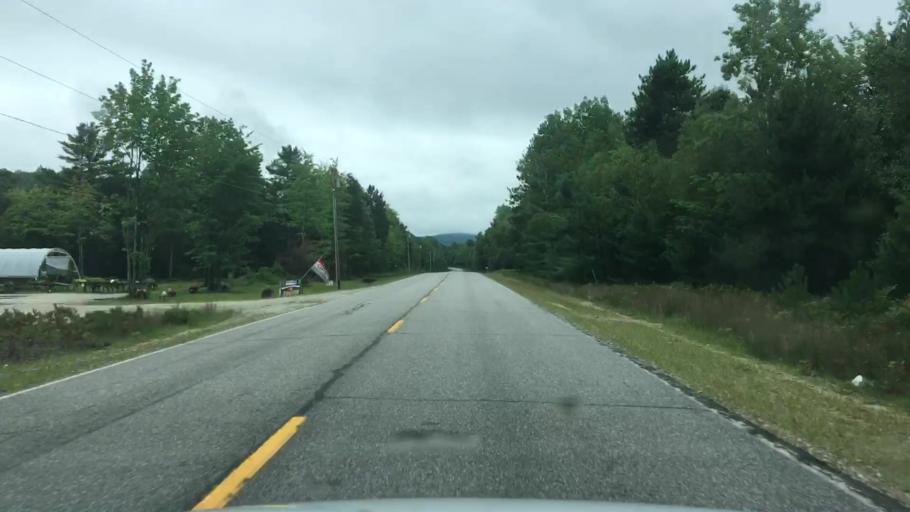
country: US
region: Maine
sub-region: Oxford County
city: Brownfield
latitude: 43.9377
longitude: -70.8856
